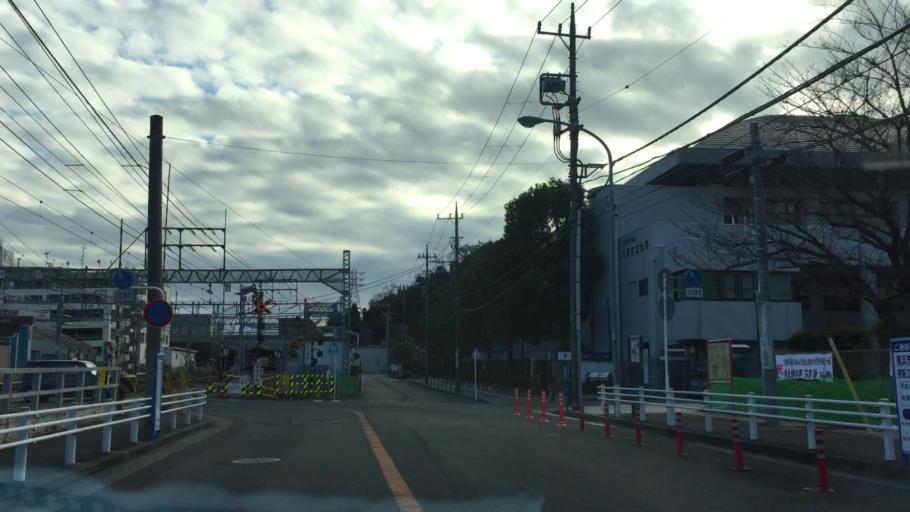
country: JP
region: Kanagawa
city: Zushi
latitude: 35.3340
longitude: 139.6199
